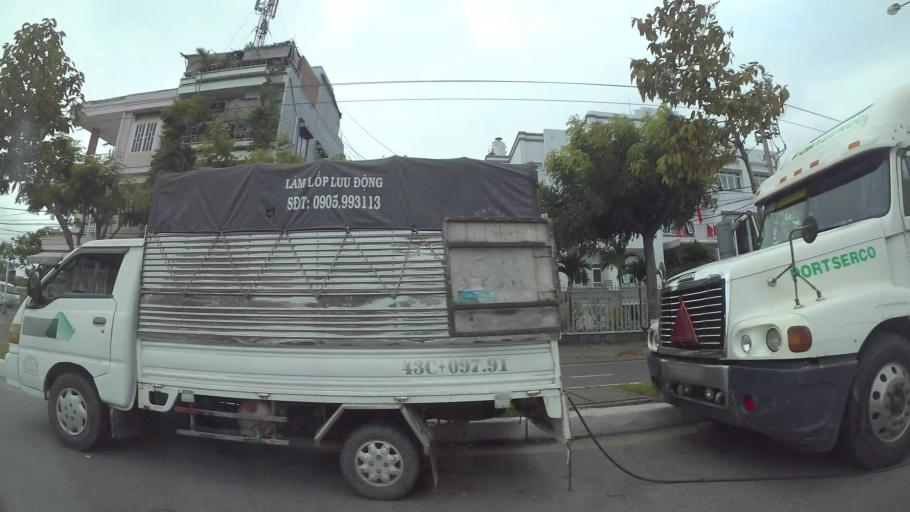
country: VN
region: Da Nang
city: Da Nang
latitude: 16.0990
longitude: 108.2463
